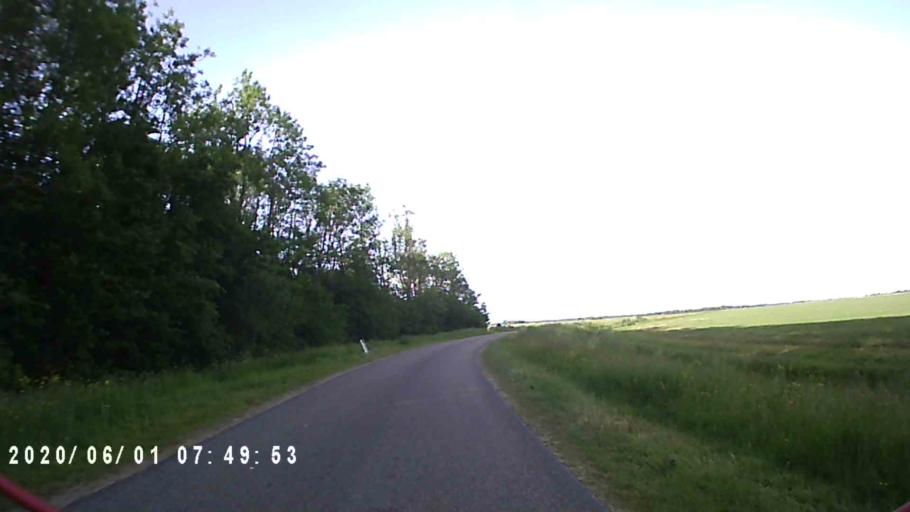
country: NL
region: Friesland
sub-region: Gemeente Dantumadiel
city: Rinsumageast
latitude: 53.2913
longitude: 5.9546
